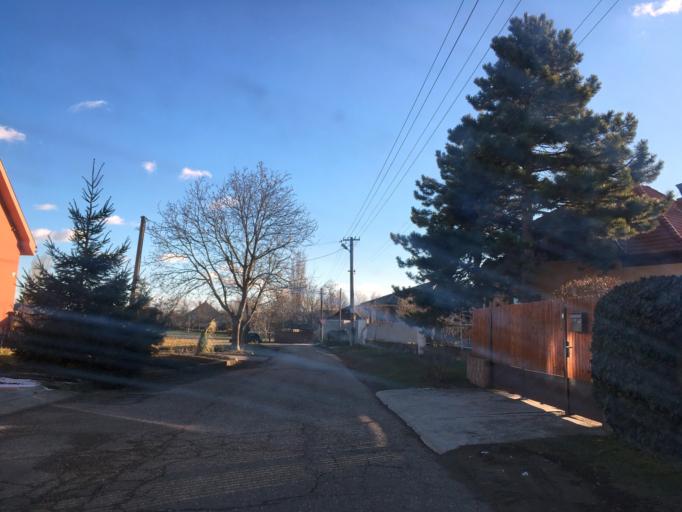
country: SK
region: Trnavsky
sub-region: Okres Dunajska Streda
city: Velky Meder
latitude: 47.8856
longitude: 17.8123
